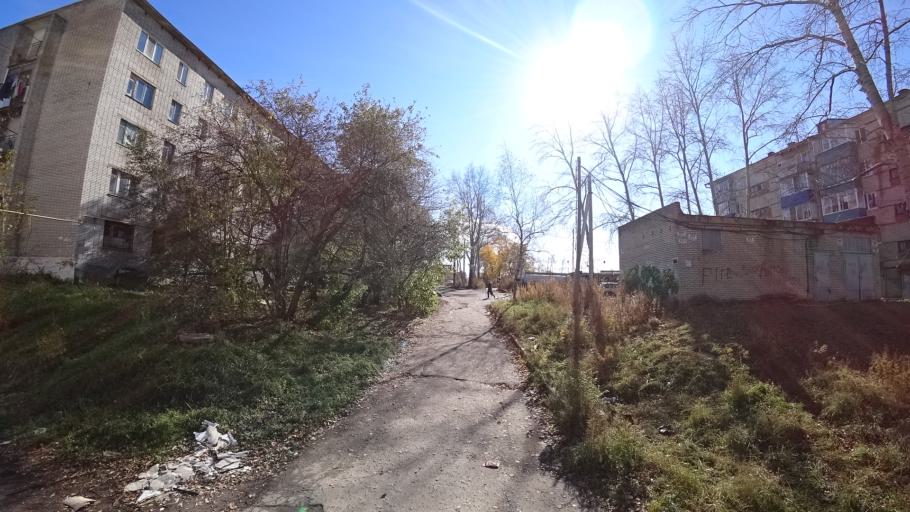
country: RU
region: Khabarovsk Krai
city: Amursk
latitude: 50.2208
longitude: 136.9022
